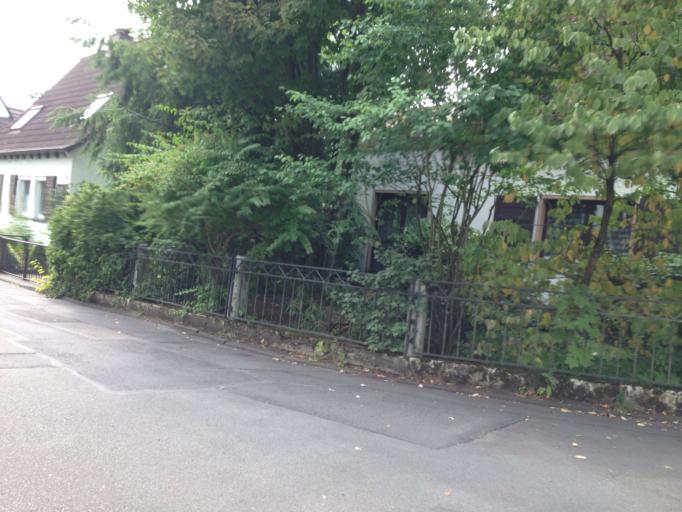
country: DE
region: Hesse
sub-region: Regierungsbezirk Giessen
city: Giessen
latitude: 50.5830
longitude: 8.7014
